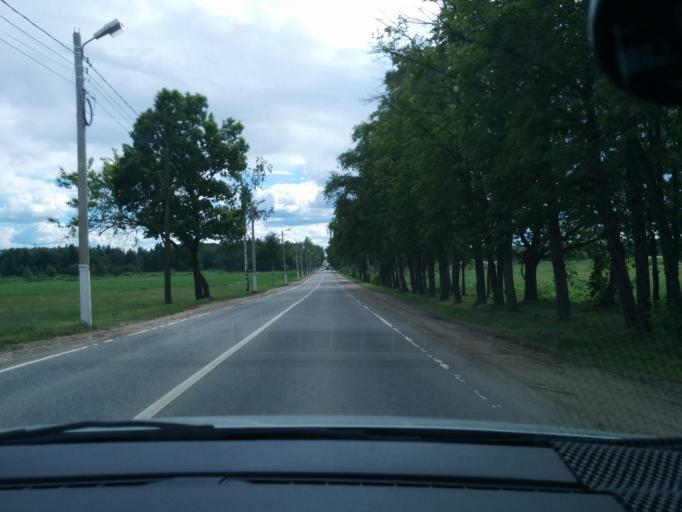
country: RU
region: Moskovskaya
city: Lugovaya
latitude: 56.0414
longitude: 37.4775
